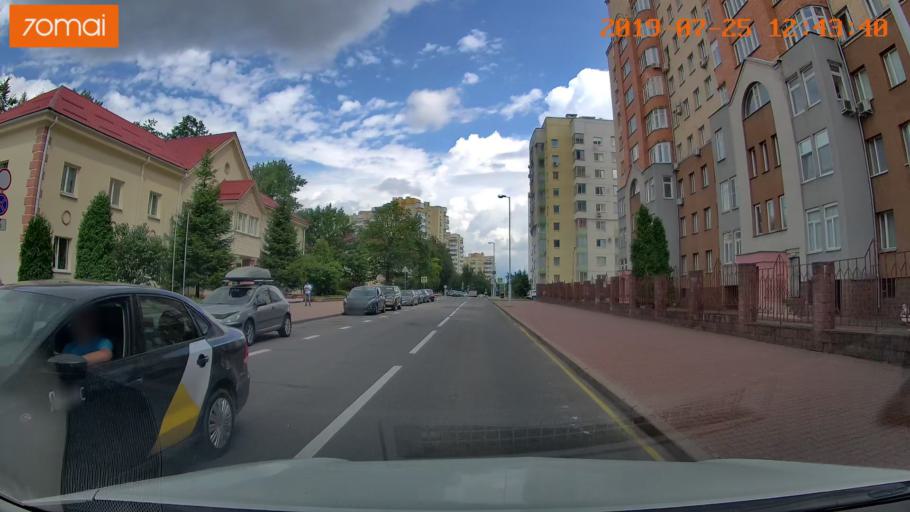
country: BY
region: Minsk
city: Minsk
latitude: 53.9142
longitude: 27.5314
